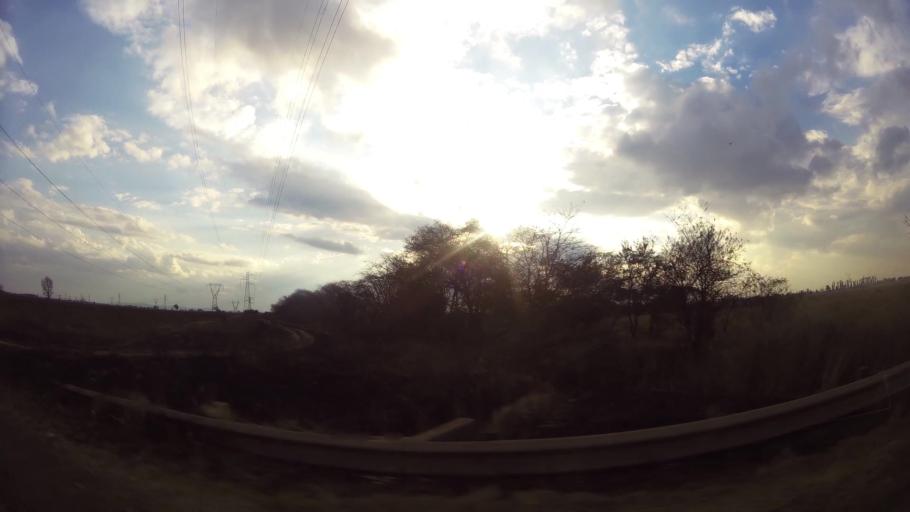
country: ZA
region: Gauteng
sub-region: Sedibeng District Municipality
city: Vanderbijlpark
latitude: -26.6640
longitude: 27.7973
